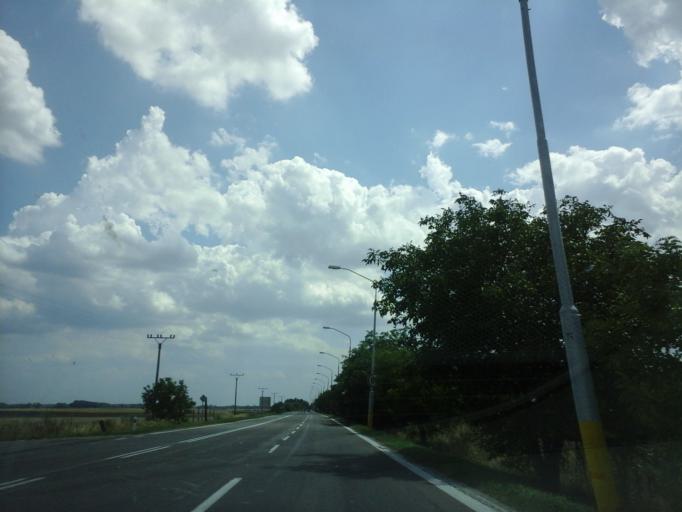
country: HU
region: Gyor-Moson-Sopron
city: Rajka
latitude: 48.0259
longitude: 17.1703
